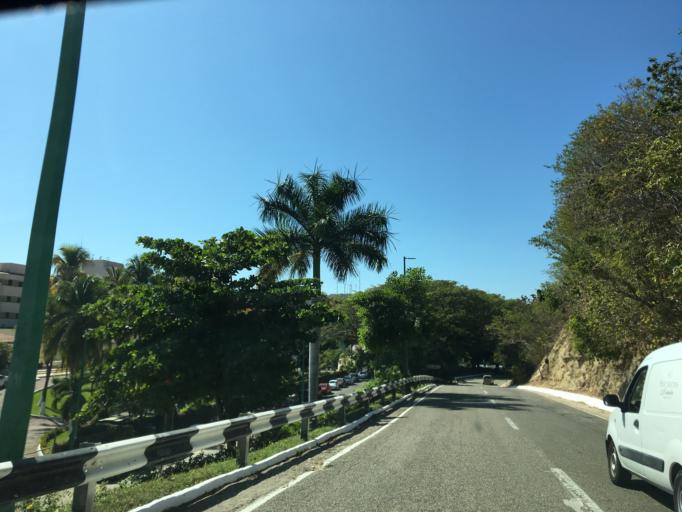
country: MX
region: Oaxaca
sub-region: Santa Maria Huatulco
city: Crucecita
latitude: 15.7755
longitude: -96.0941
